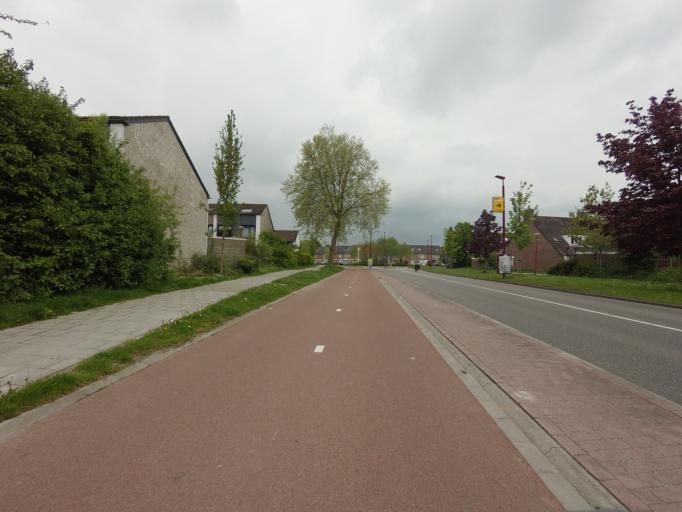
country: NL
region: Utrecht
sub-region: Gemeente Nieuwegein
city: Nieuwegein
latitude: 52.0316
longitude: 5.0741
